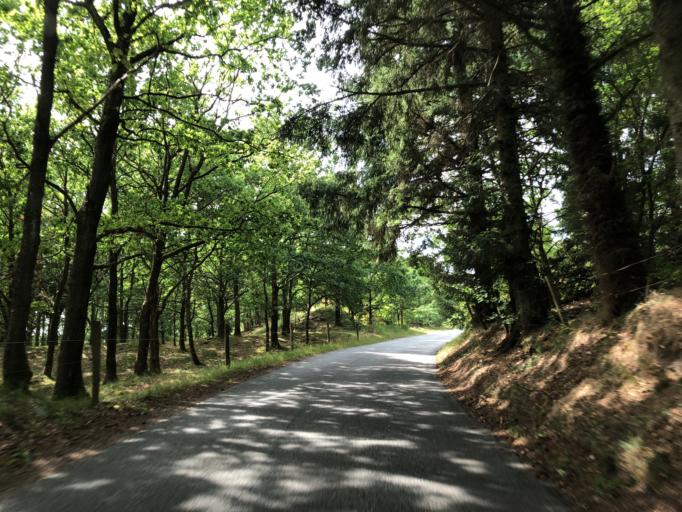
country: DK
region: South Denmark
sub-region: Vejle Kommune
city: Egtved
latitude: 55.6462
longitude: 9.2576
